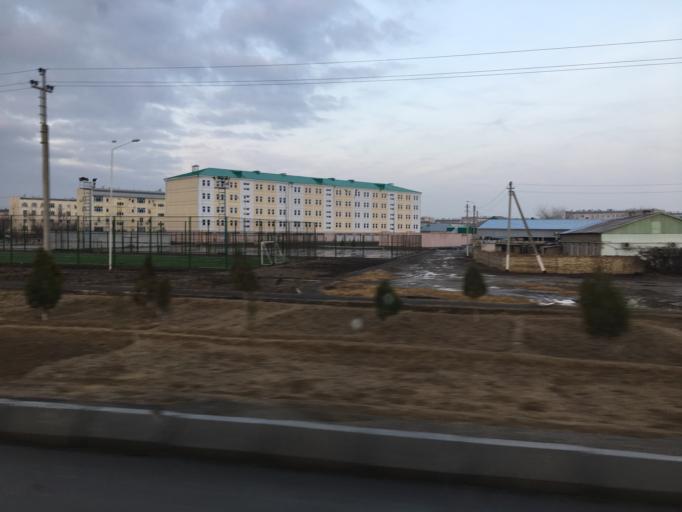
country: TM
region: Mary
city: Mary
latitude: 37.5812
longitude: 61.8362
